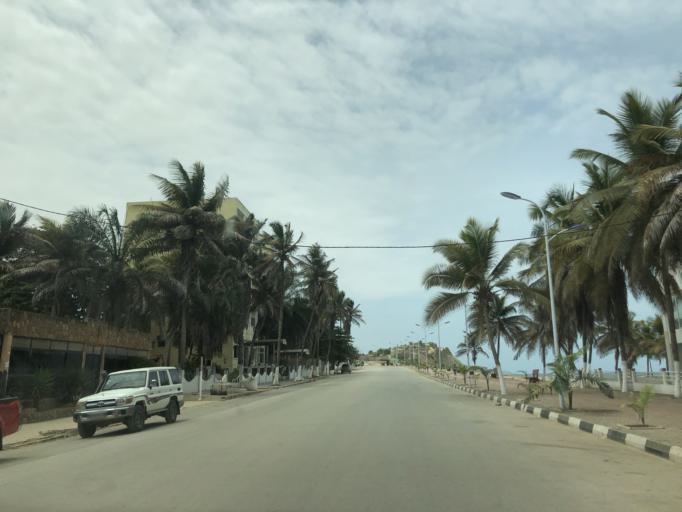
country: AO
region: Cuanza Sul
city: Sumbe
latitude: -11.1989
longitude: 13.8353
